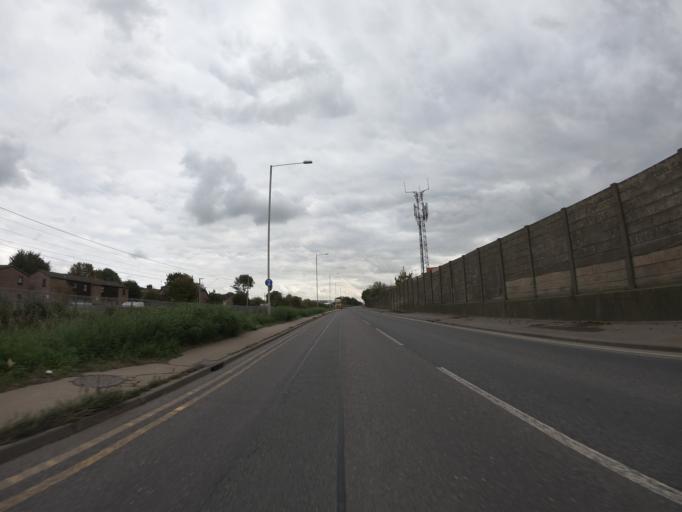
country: GB
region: England
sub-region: Borough of Thurrock
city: Tilbury
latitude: 51.4608
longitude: 0.3565
